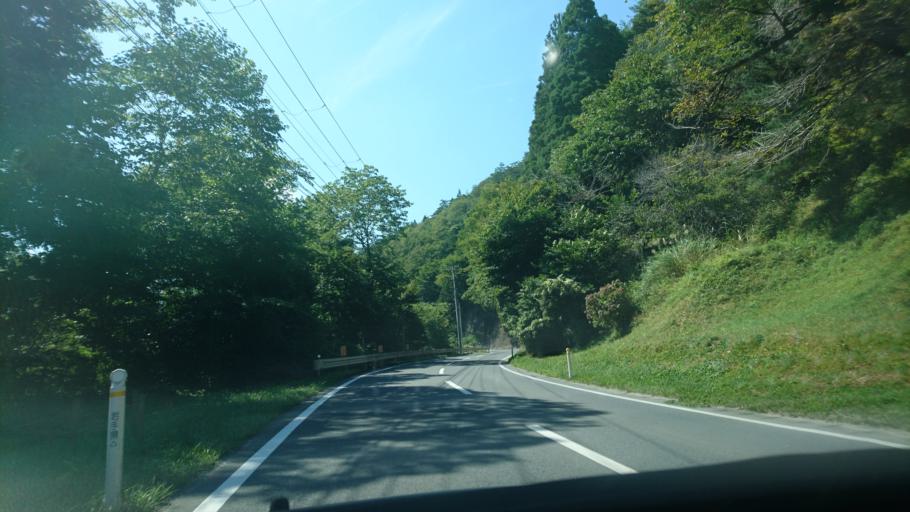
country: JP
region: Iwate
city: Ofunato
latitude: 39.0240
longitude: 141.5637
